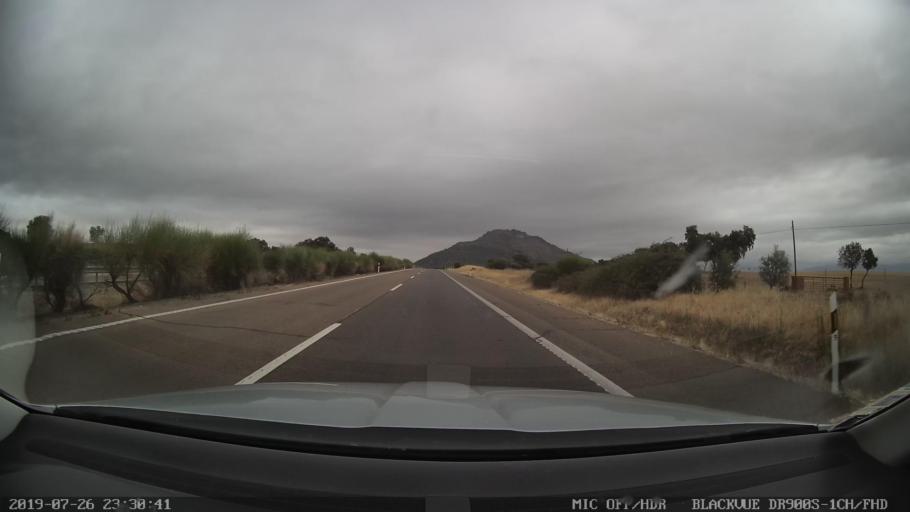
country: ES
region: Extremadura
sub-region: Provincia de Caceres
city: Puerto de Santa Cruz
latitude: 39.2841
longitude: -5.8557
